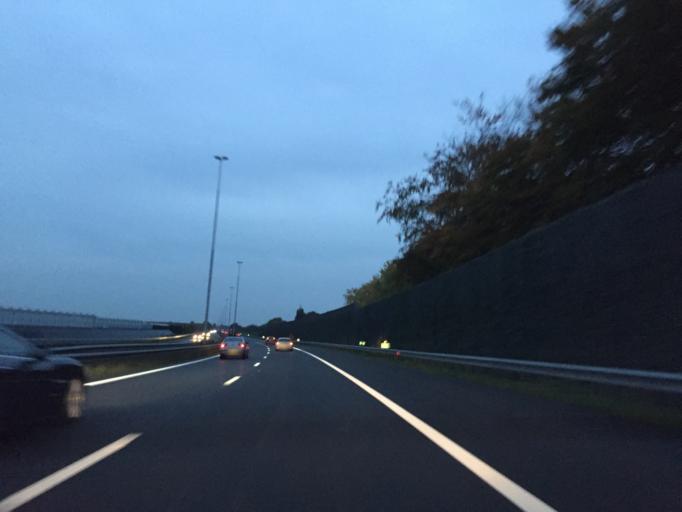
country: NL
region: North Brabant
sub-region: Gemeente Heusden
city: Heusden
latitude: 51.6920
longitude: 5.1182
